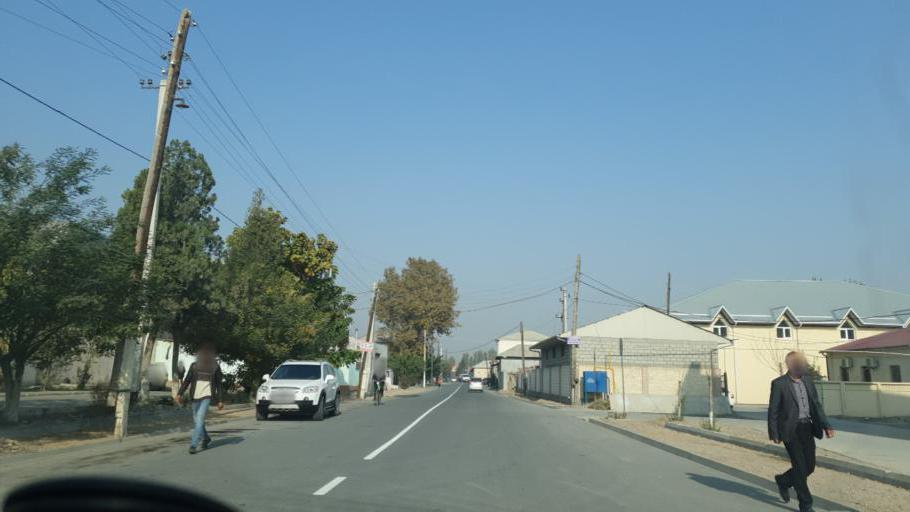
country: UZ
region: Fergana
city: Qo`qon
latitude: 40.5793
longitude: 70.9139
